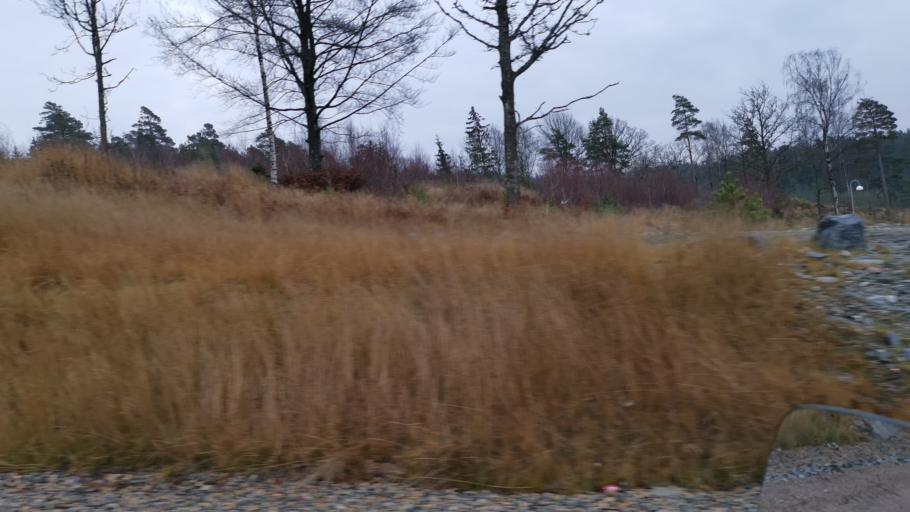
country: SE
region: Vaestra Goetaland
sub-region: Orust
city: Henan
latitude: 58.3483
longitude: 11.7007
